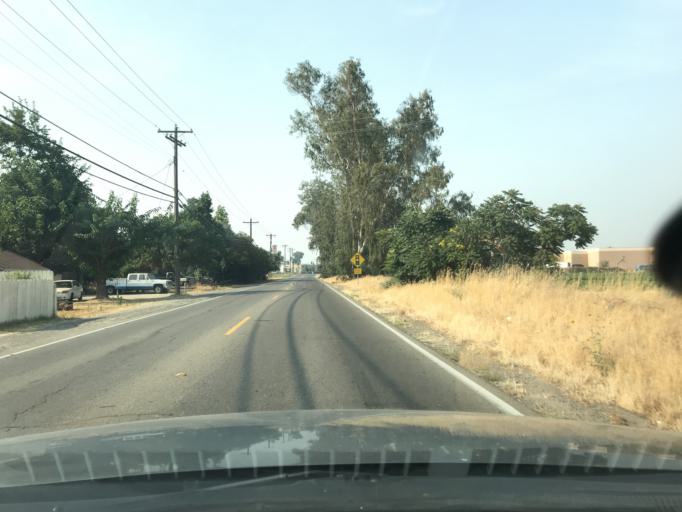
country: US
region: California
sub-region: Merced County
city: Atwater
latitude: 37.3395
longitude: -120.6144
